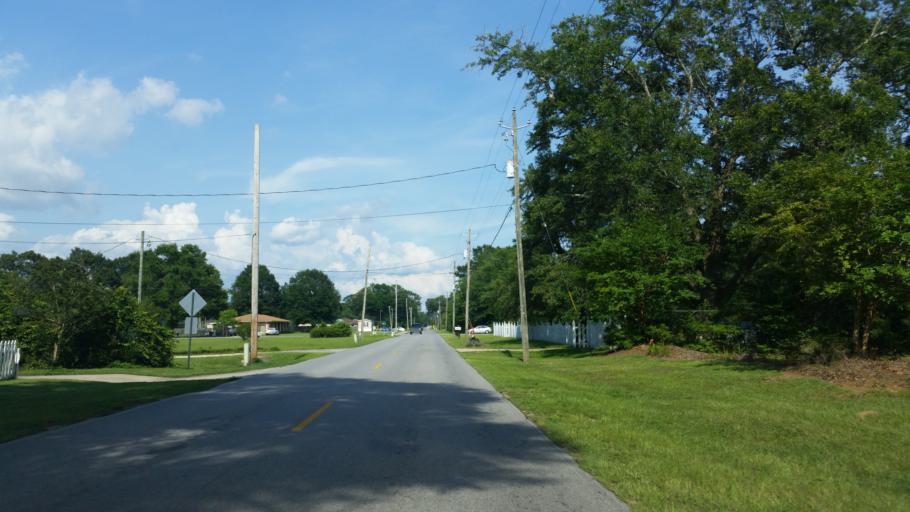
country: US
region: Florida
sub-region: Escambia County
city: Ensley
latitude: 30.5409
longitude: -87.2891
